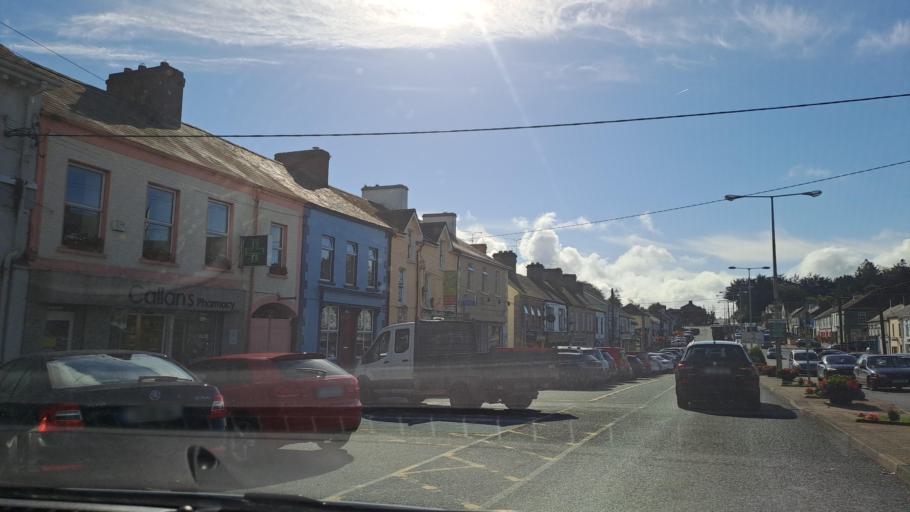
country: IE
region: Ulster
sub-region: An Cabhan
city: Kingscourt
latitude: 53.9061
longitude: -6.8050
